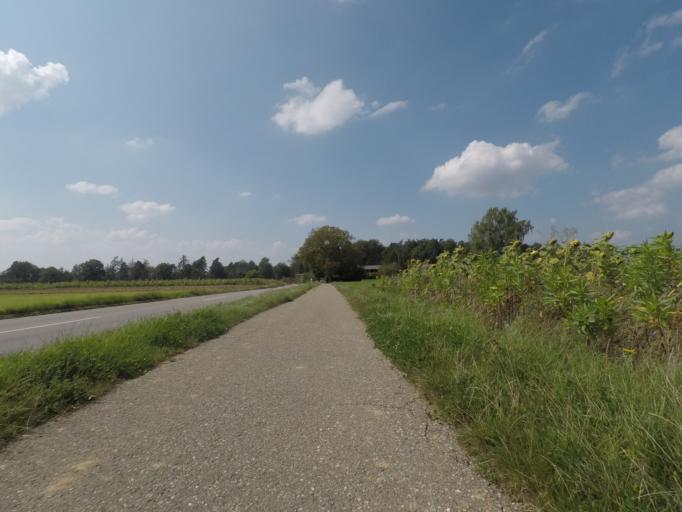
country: DE
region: Baden-Wuerttemberg
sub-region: Regierungsbezirk Stuttgart
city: Winterbach
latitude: 48.7852
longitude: 9.4454
